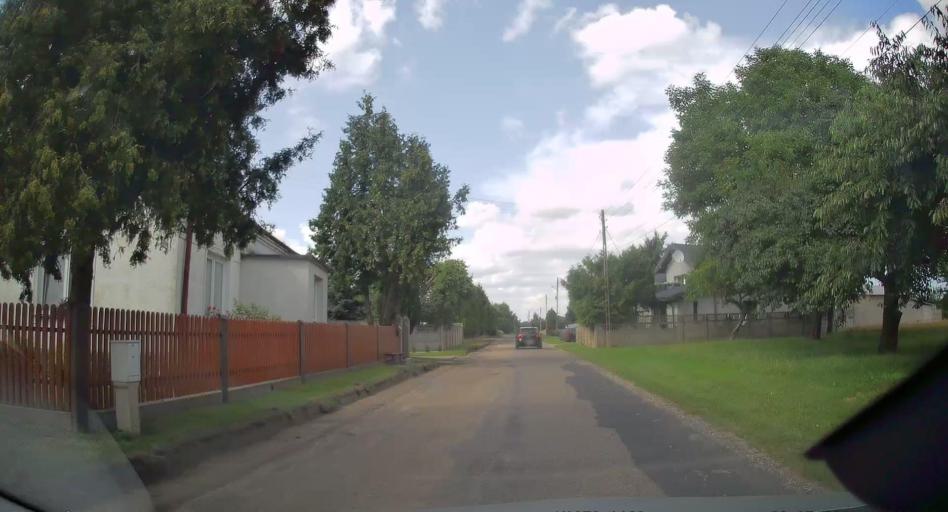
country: PL
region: Lodz Voivodeship
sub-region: Powiat brzezinski
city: Rogow
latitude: 51.8097
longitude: 19.8957
